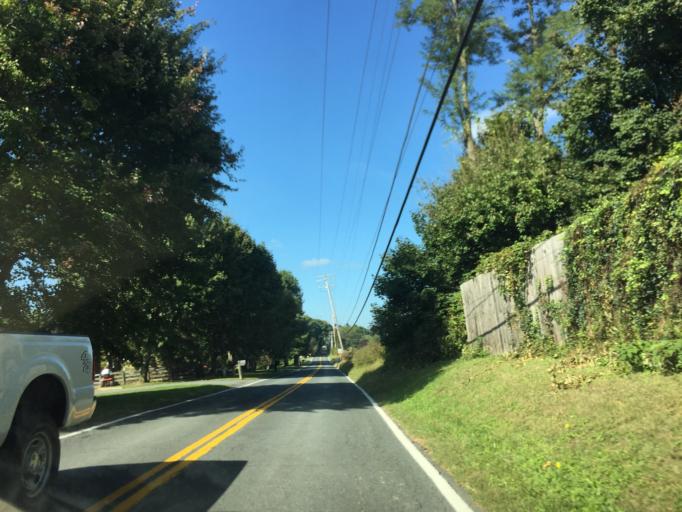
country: US
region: Maryland
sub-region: Harford County
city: Fallston
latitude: 39.5596
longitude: -76.4221
